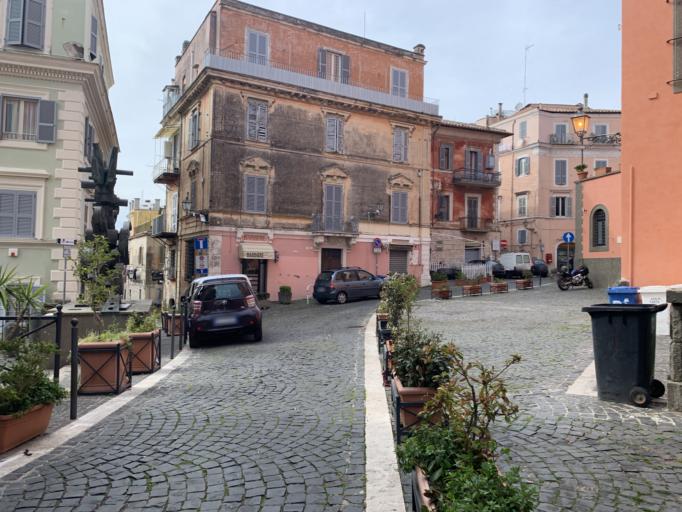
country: IT
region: Latium
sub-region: Citta metropolitana di Roma Capitale
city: Castel Gandolfo
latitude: 41.7695
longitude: 12.6584
